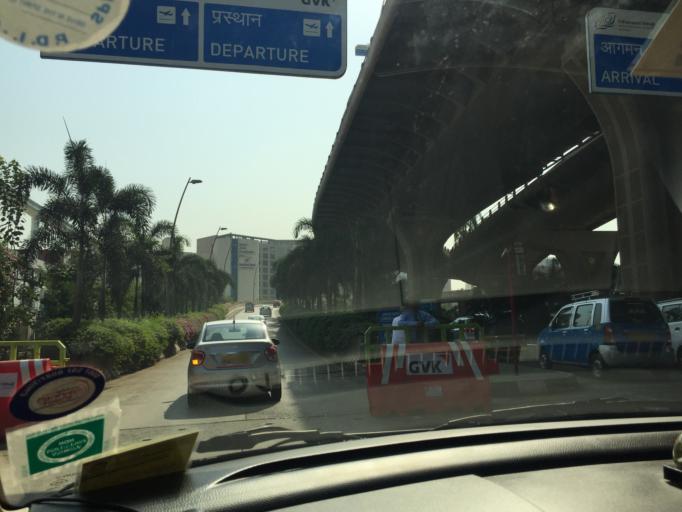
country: IN
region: Maharashtra
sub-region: Mumbai Suburban
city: Mumbai
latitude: 19.1033
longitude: 72.8751
